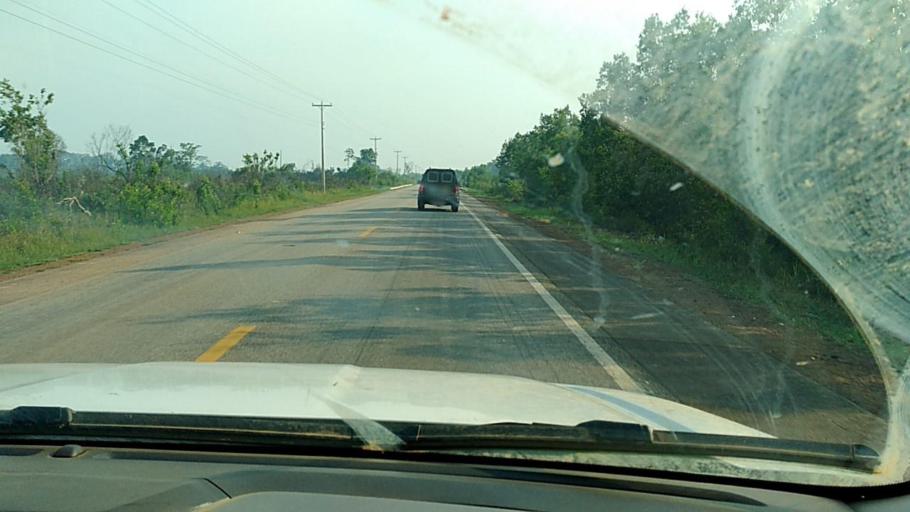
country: BR
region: Rondonia
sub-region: Porto Velho
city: Porto Velho
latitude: -8.4656
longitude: -63.9732
